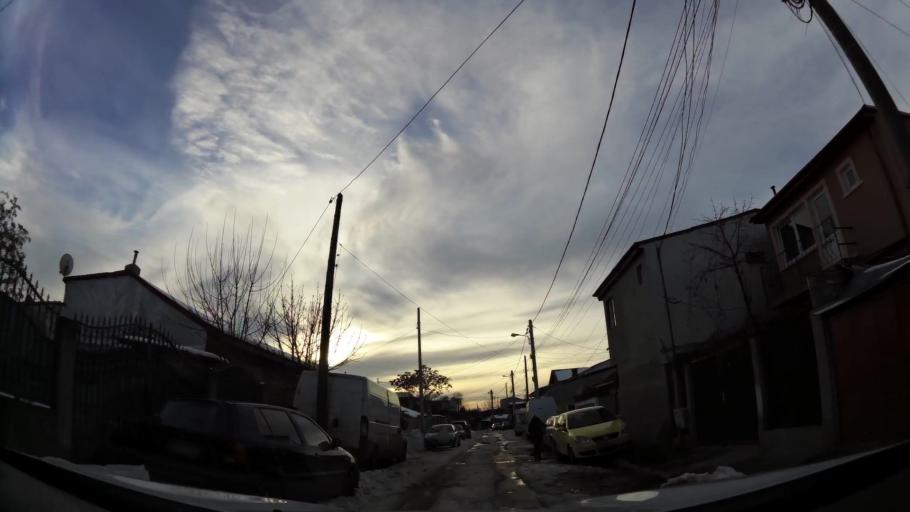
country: RO
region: Bucuresti
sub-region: Municipiul Bucuresti
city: Bucuresti
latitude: 44.3951
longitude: 26.0762
